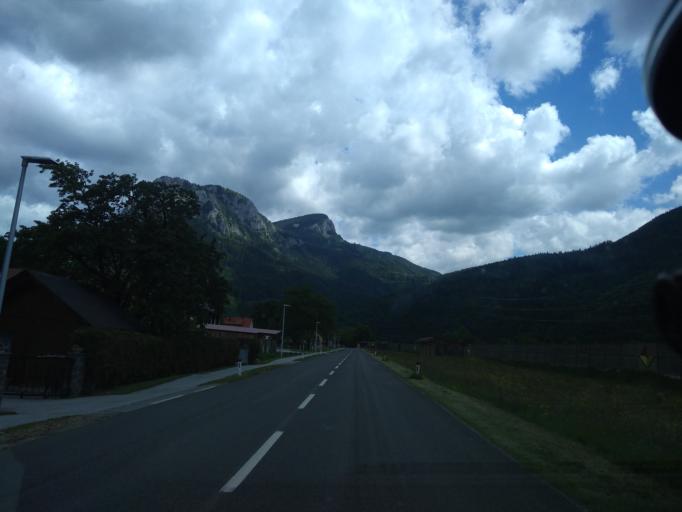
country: AT
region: Styria
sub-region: Politischer Bezirk Graz-Umgebung
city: Rothelstein
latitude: 47.3049
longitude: 15.3660
